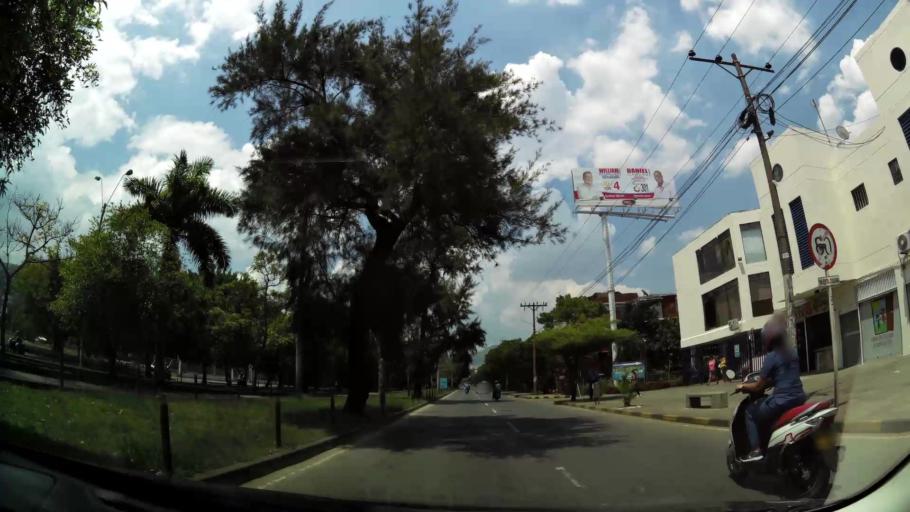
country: CO
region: Valle del Cauca
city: Cali
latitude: 3.4165
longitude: -76.5482
